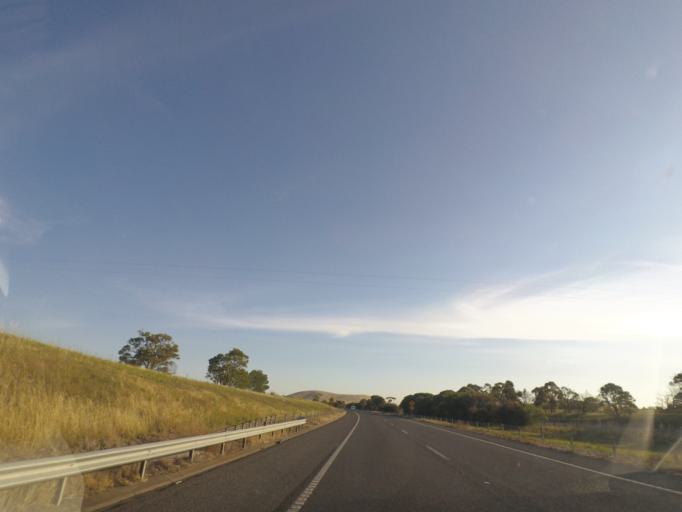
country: AU
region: Victoria
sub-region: Whittlesea
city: Whittlesea
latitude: -37.4356
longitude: 144.9819
